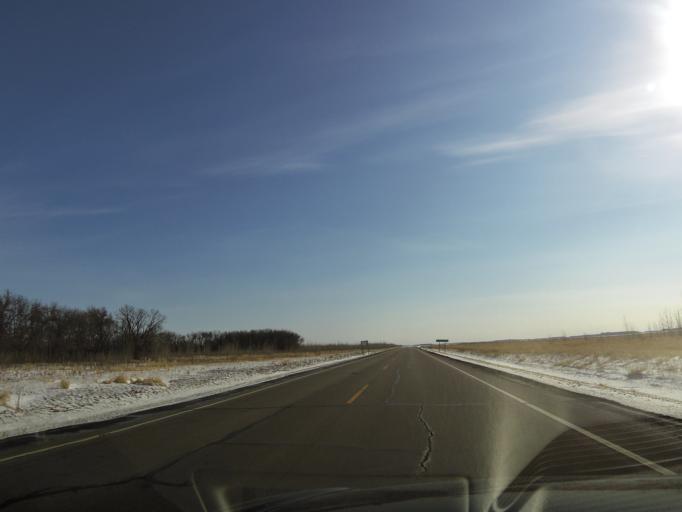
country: US
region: North Dakota
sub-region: Walsh County
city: Grafton
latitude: 48.4118
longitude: -97.1069
